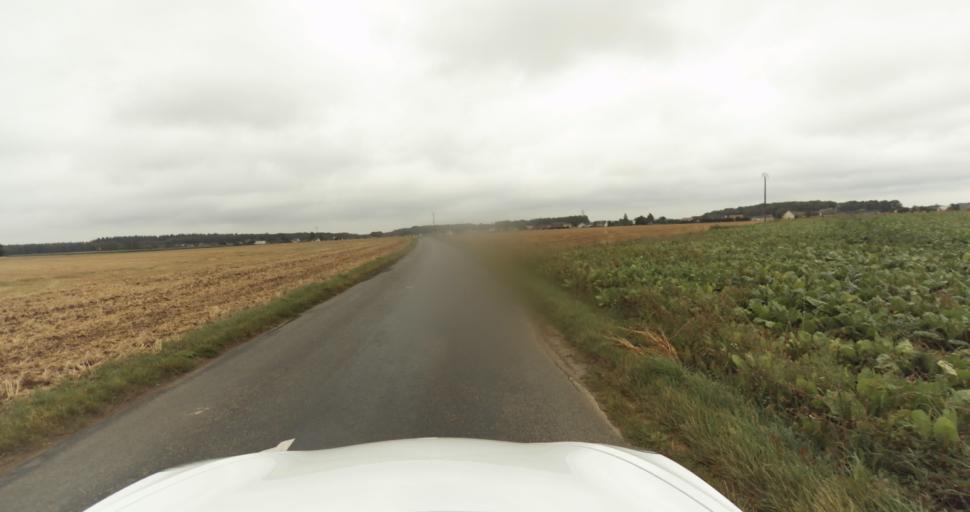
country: FR
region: Haute-Normandie
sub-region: Departement de l'Eure
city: Aviron
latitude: 49.0657
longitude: 1.1192
